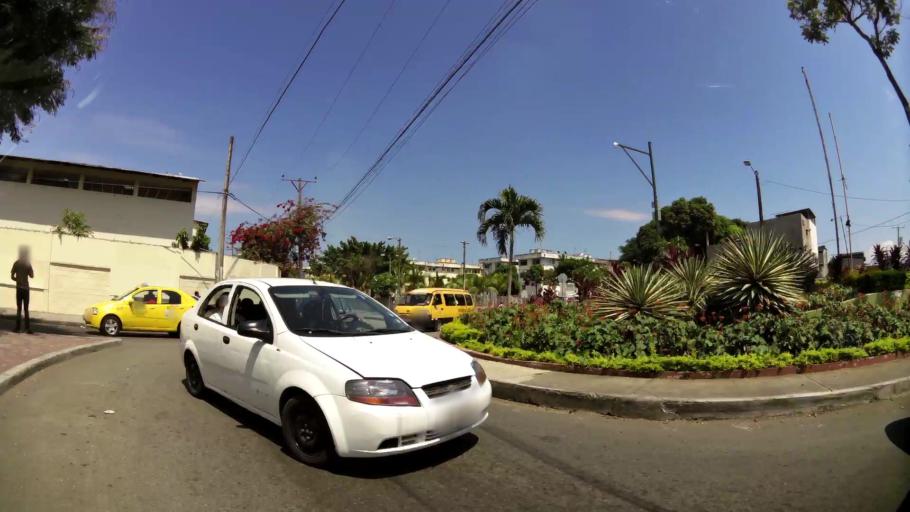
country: EC
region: Guayas
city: Guayaquil
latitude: -2.2320
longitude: -79.9019
